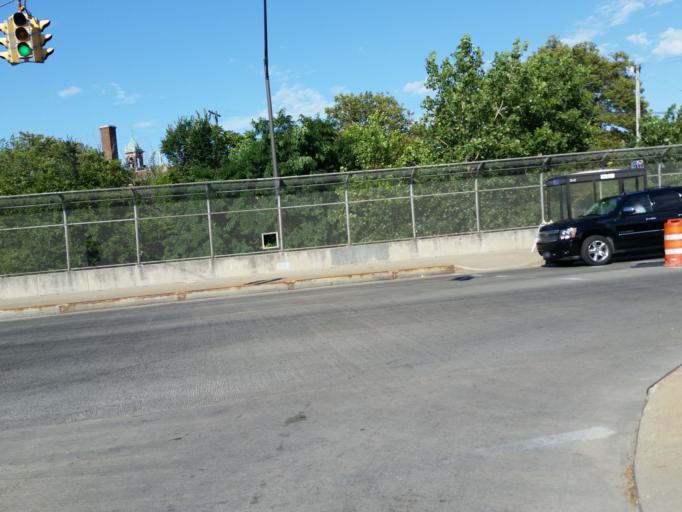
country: US
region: Ohio
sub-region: Cuyahoga County
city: Cleveland
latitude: 41.4813
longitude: -81.7013
